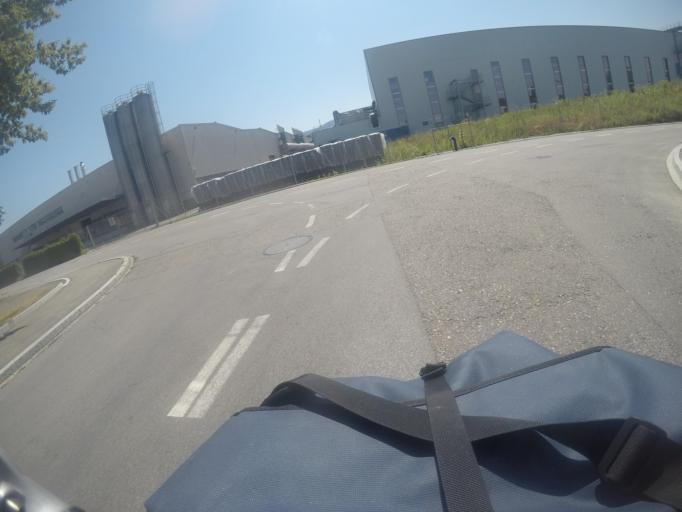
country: CH
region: Saint Gallen
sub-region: Wahlkreis Rorschach
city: Goldach
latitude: 47.4848
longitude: 9.4703
